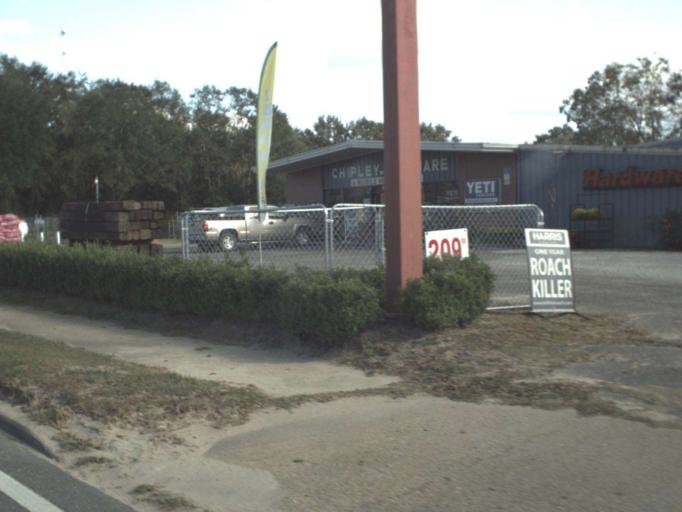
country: US
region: Florida
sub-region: Washington County
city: Chipley
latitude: 30.7801
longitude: -85.5313
